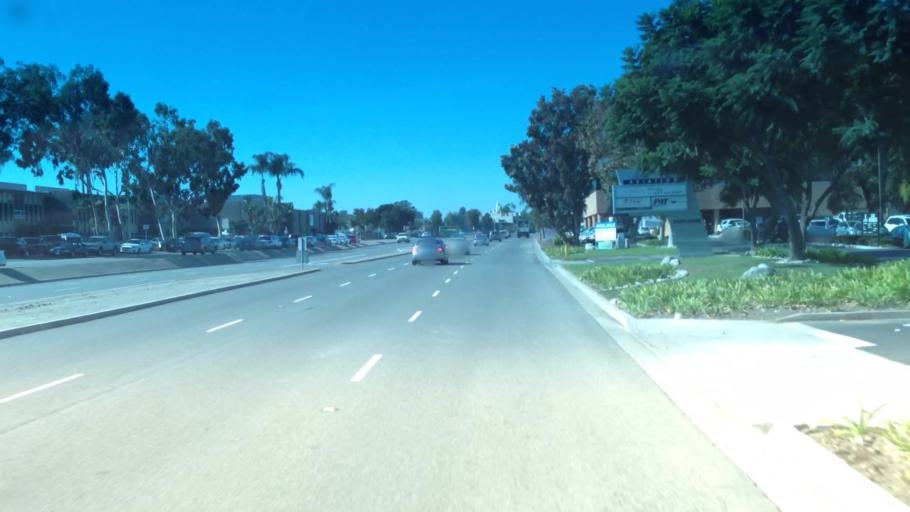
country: US
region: California
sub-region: Los Angeles County
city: Signal Hill
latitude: 33.8107
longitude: -118.1526
